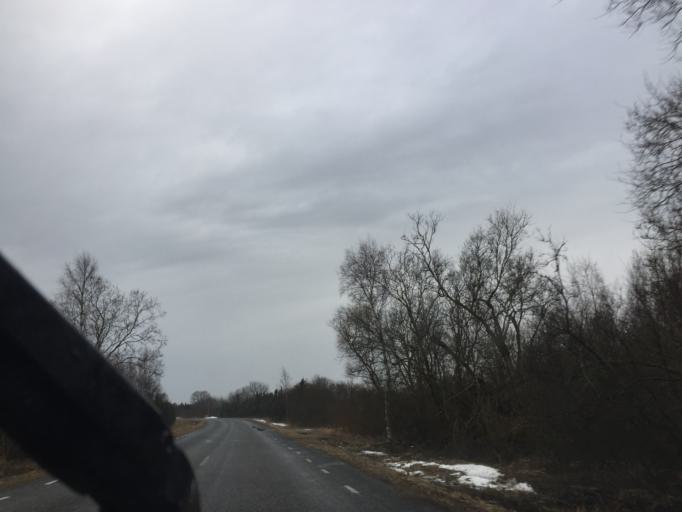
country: EE
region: Saare
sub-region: Orissaare vald
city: Orissaare
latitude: 58.5759
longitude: 23.0289
